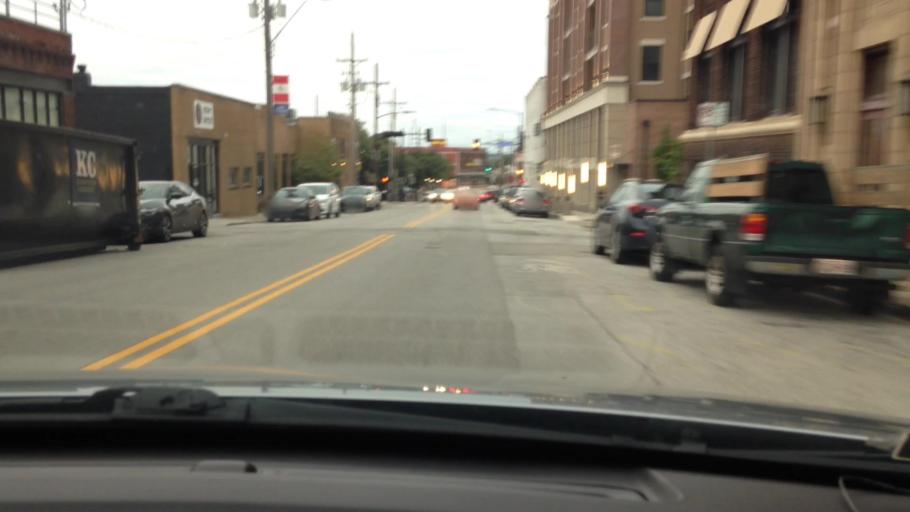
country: US
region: Missouri
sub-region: Jackson County
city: Kansas City
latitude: 39.1079
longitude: -94.5802
